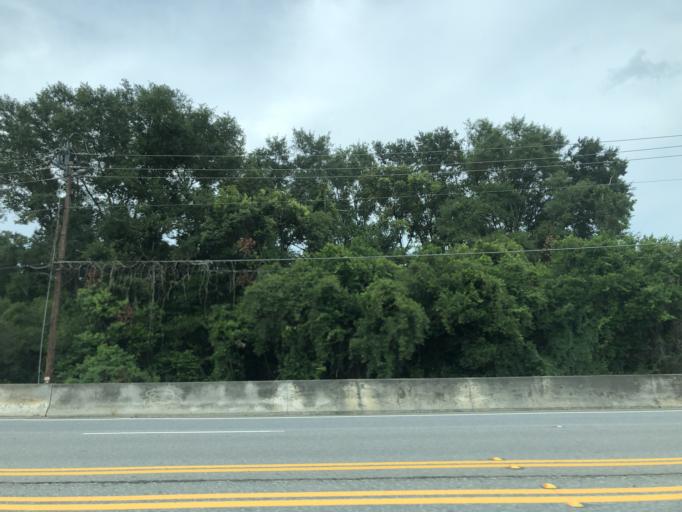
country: US
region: Georgia
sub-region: Wayne County
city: Jesup
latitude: 31.6059
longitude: -81.8791
